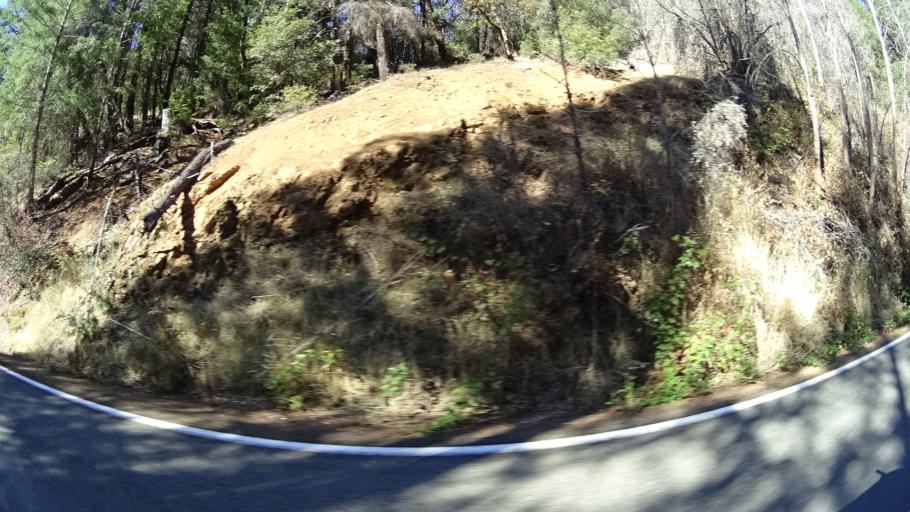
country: US
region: California
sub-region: Trinity County
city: Weaverville
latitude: 41.1931
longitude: -123.0732
